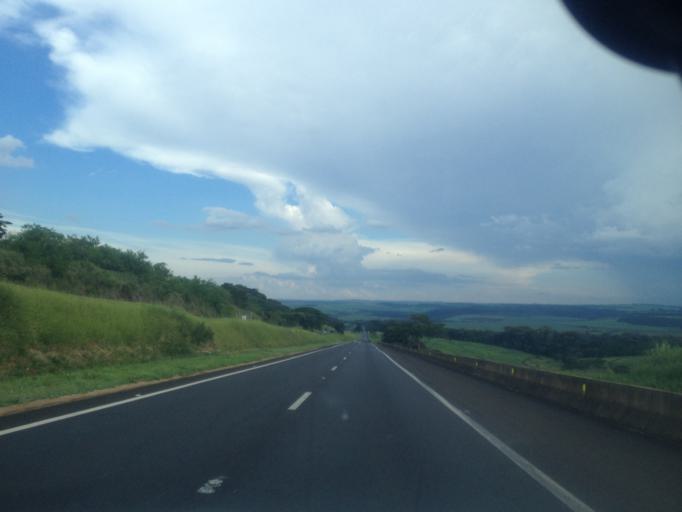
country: BR
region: Sao Paulo
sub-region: Santa Rita Do Passa Quatro
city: Santa Rita do Passa Quatro
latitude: -21.7044
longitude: -47.5948
